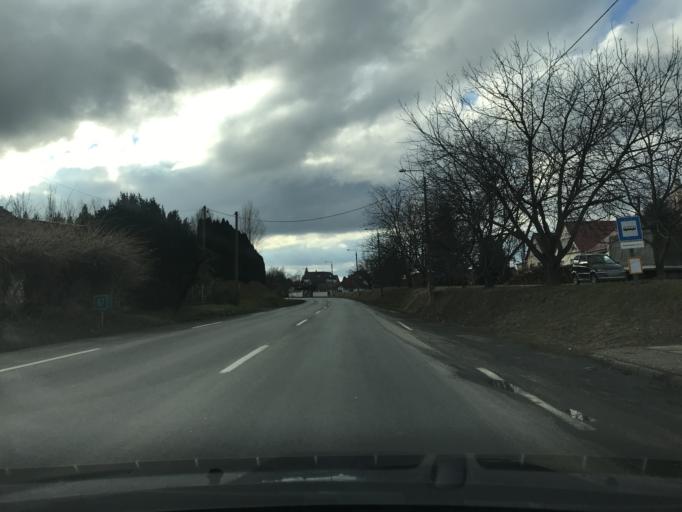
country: HU
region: Bacs-Kiskun
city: Nemesnadudvar
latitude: 46.3329
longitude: 19.0587
